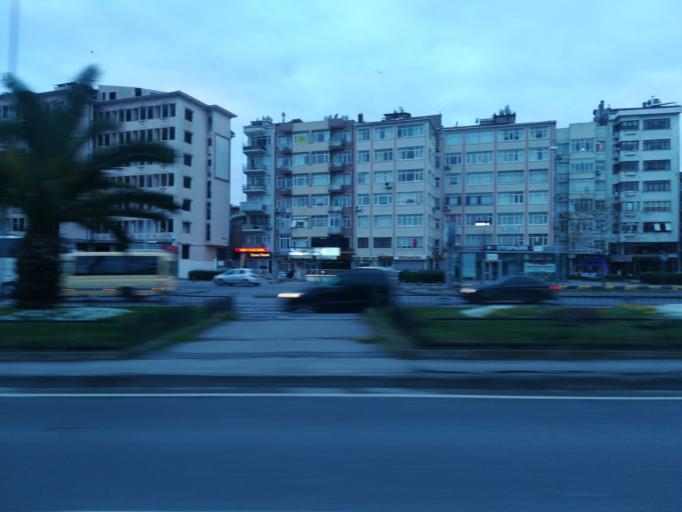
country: TR
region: Istanbul
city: Istanbul
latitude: 41.0131
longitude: 28.9460
